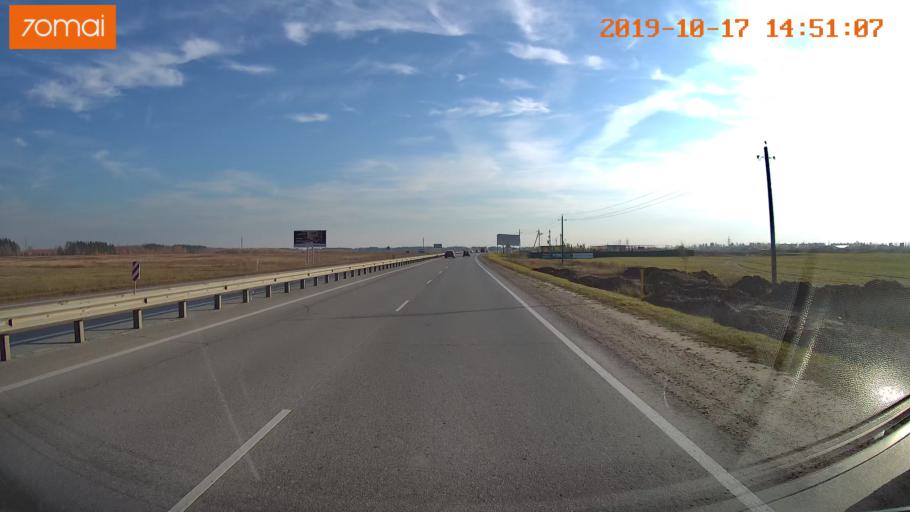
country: RU
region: Rjazan
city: Polyany
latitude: 54.7243
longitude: 39.8466
